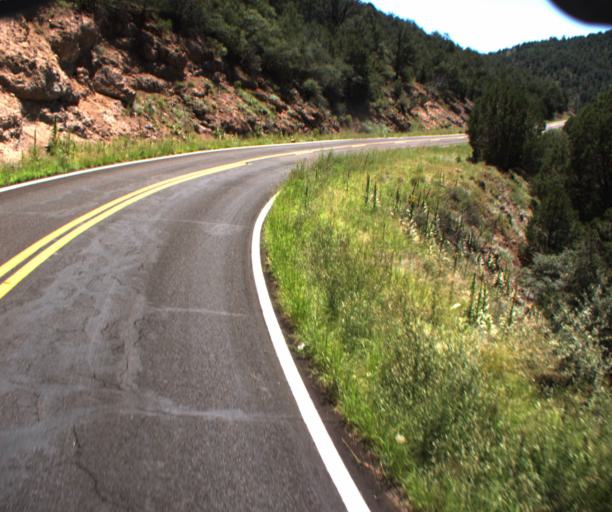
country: US
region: Arizona
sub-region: Greenlee County
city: Morenci
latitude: 33.4145
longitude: -109.3616
